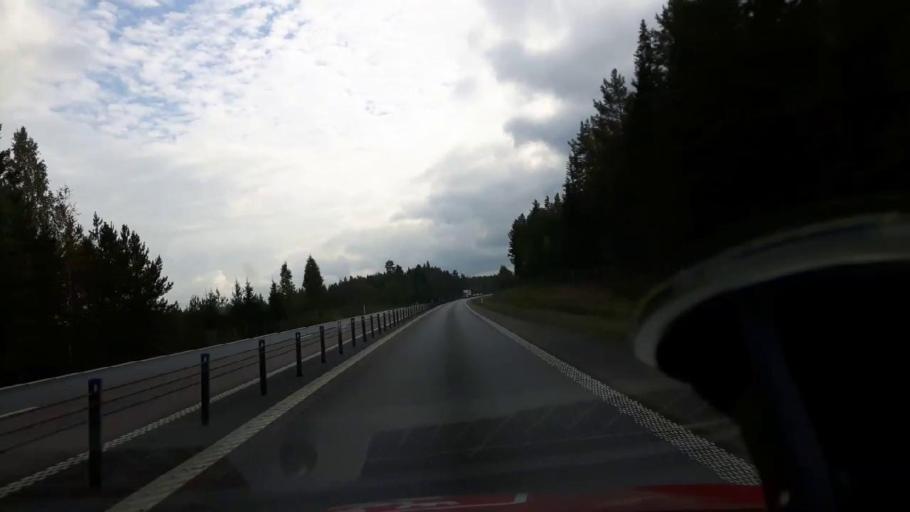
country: SE
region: Gaevleborg
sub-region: Gavle Kommun
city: Norrsundet
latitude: 60.8877
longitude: 17.0401
